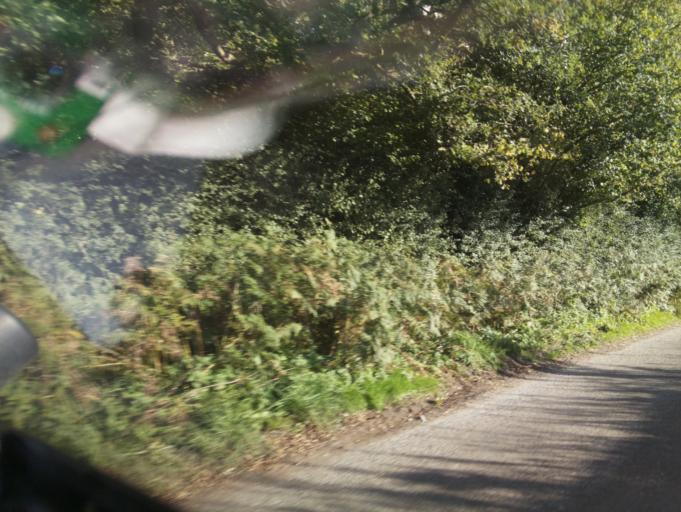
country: GB
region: England
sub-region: Hampshire
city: Four Marks
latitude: 51.0524
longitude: -1.0386
